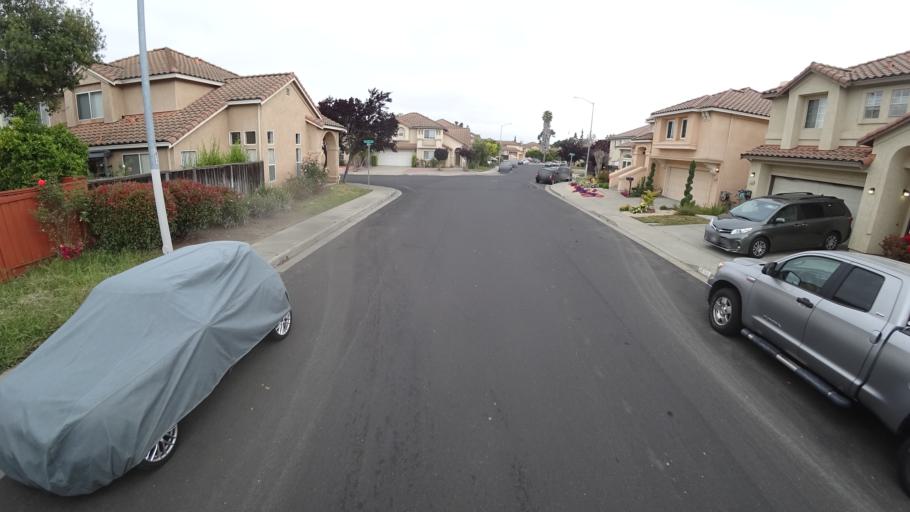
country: US
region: California
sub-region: Alameda County
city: Cherryland
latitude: 37.6403
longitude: -122.1115
